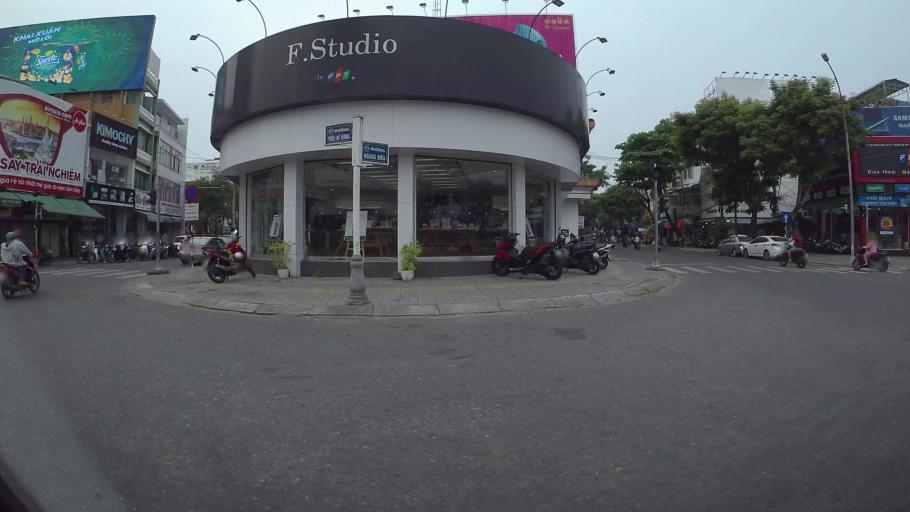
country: VN
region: Da Nang
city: Da Nang
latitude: 16.0609
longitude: 108.2171
